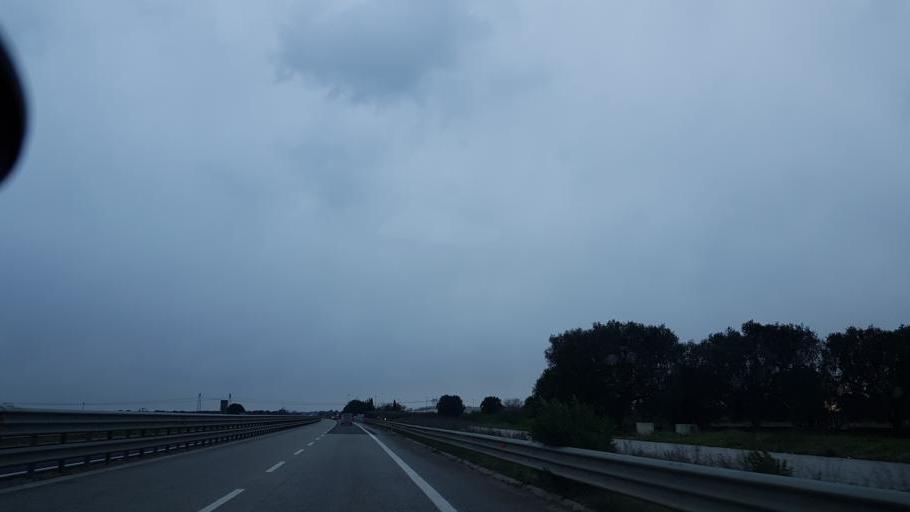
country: IT
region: Apulia
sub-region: Provincia di Brindisi
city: Mesagne
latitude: 40.5842
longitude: 17.8480
